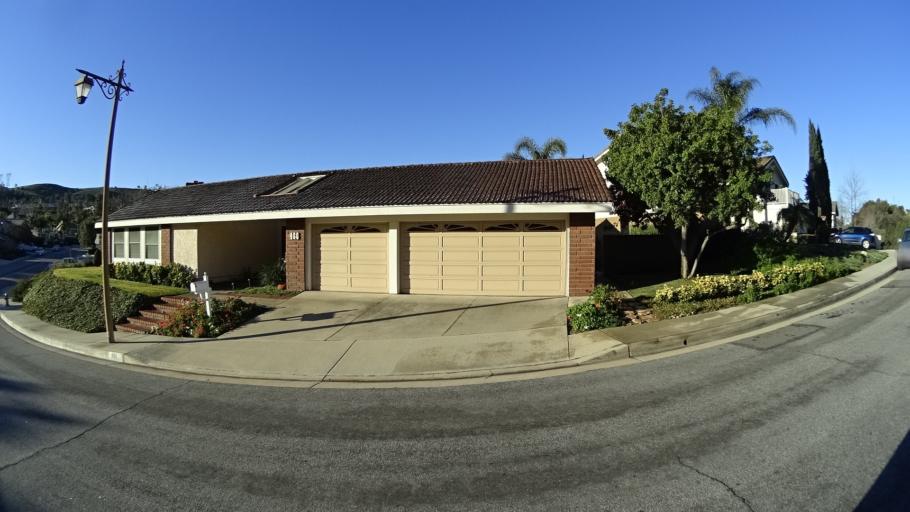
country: US
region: California
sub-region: Orange County
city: Villa Park
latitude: 33.8447
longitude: -117.7937
